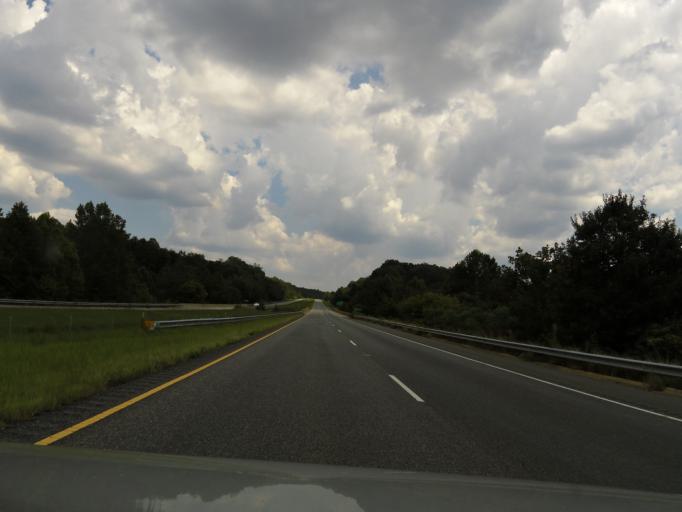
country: US
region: North Carolina
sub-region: Rutherford County
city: Rutherfordton
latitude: 35.2872
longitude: -82.0315
